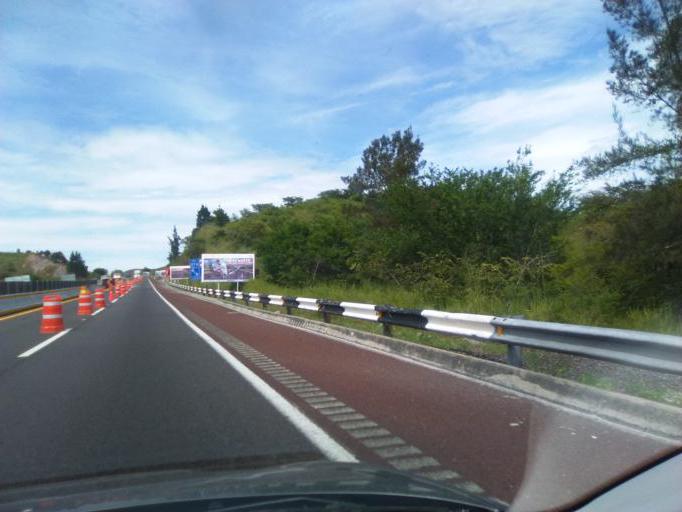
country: MX
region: Guerrero
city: Mazatlan
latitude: 17.4160
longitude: -99.4644
